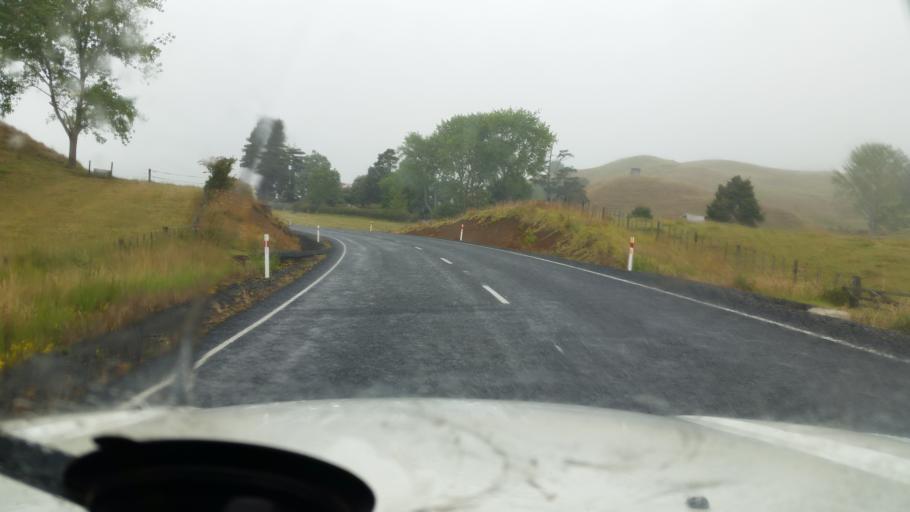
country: NZ
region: Northland
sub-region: Far North District
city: Kaitaia
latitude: -35.2760
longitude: 173.3479
